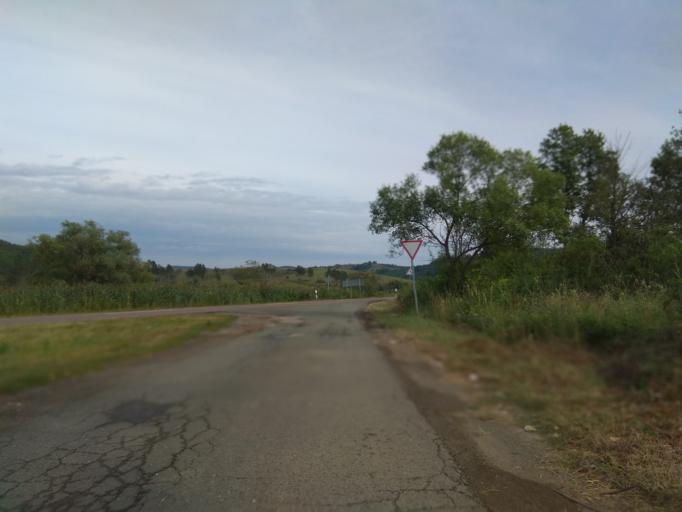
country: HU
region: Heves
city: Belapatfalva
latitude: 48.0271
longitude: 20.2886
